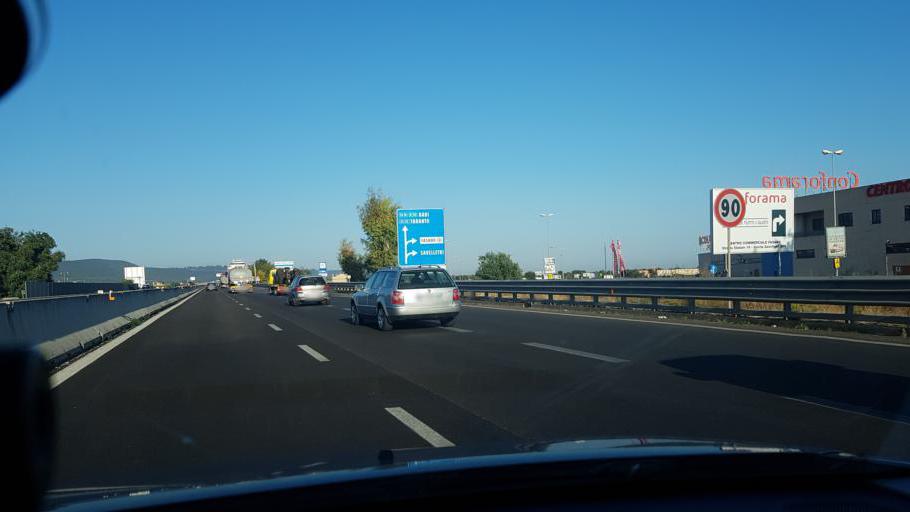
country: IT
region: Apulia
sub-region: Provincia di Brindisi
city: Fasano
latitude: 40.8383
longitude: 17.3792
